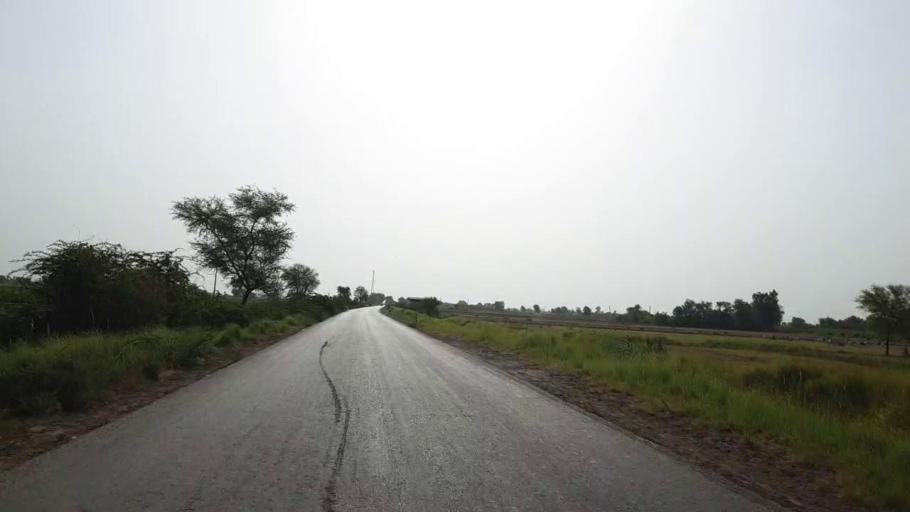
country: PK
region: Sindh
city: Nawabshah
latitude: 26.2672
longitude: 68.5149
